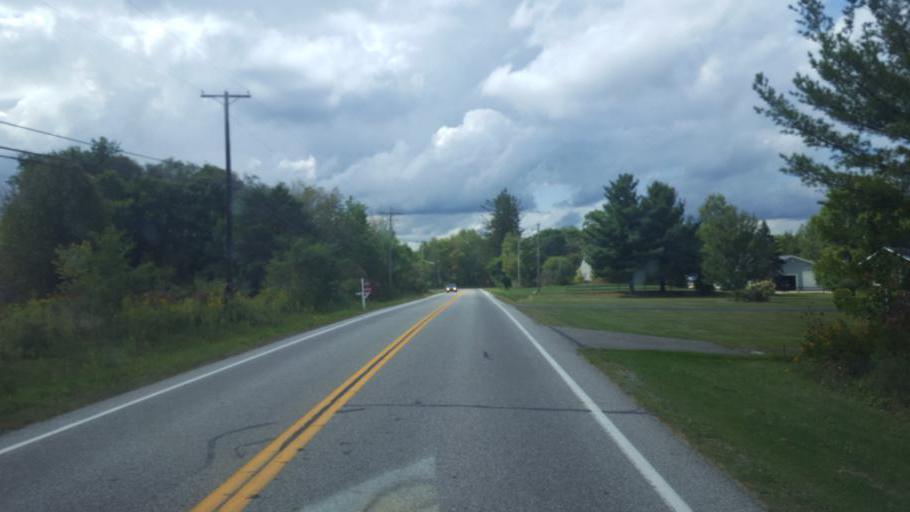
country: US
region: Ohio
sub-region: Geauga County
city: Burton
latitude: 41.4538
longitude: -81.1266
